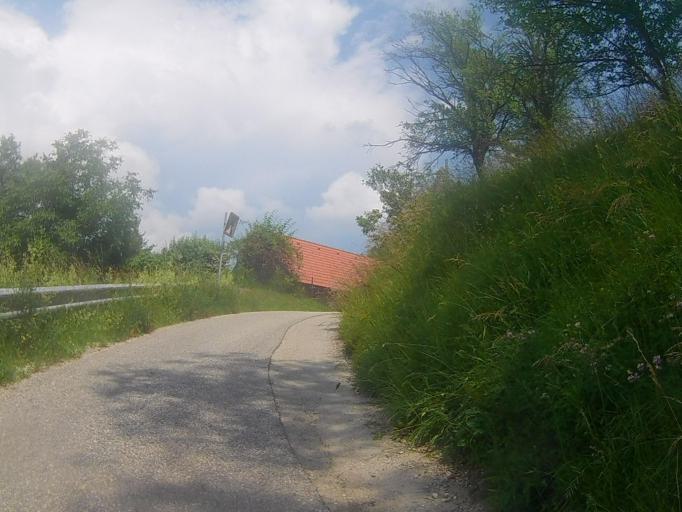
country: SI
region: Maribor
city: Bresternica
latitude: 46.5834
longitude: 15.5928
